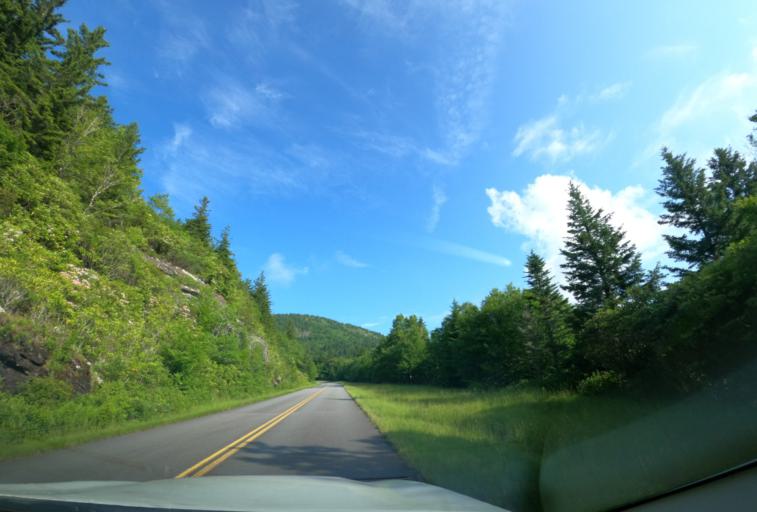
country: US
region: North Carolina
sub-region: Haywood County
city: Hazelwood
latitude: 35.2982
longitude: -82.9204
